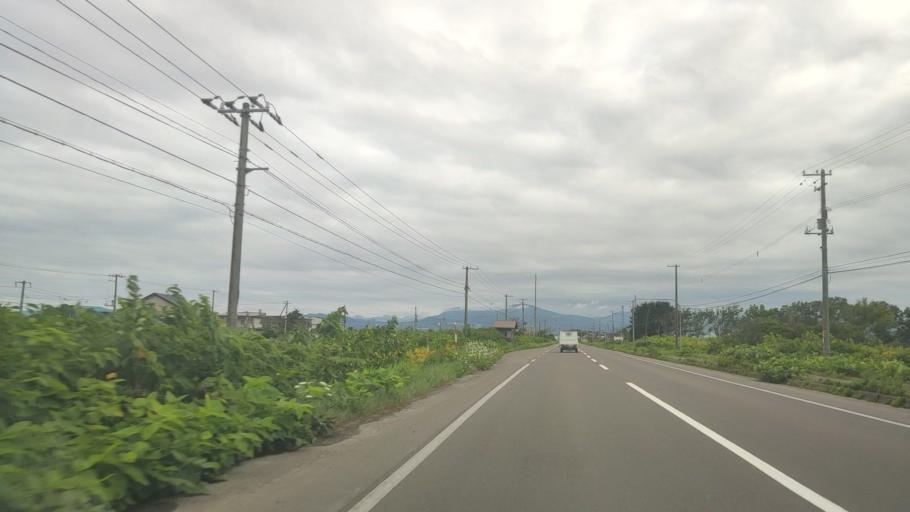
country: JP
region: Hokkaido
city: Nanae
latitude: 42.3191
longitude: 140.2751
